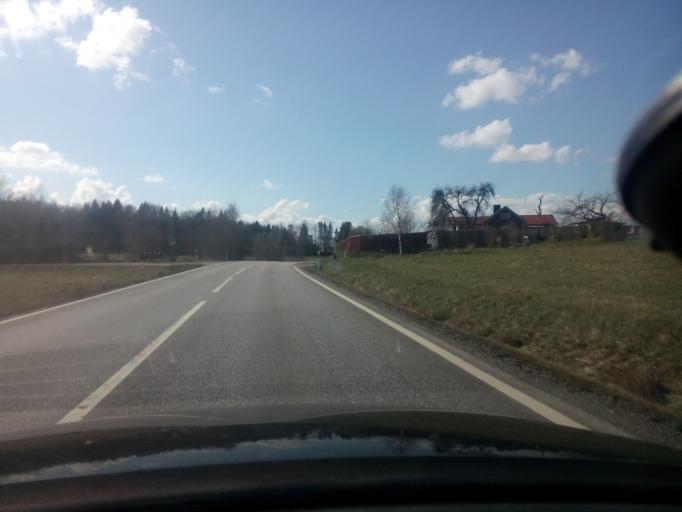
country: SE
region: Soedermanland
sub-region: Flens Kommun
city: Malmkoping
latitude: 59.1033
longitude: 16.7798
